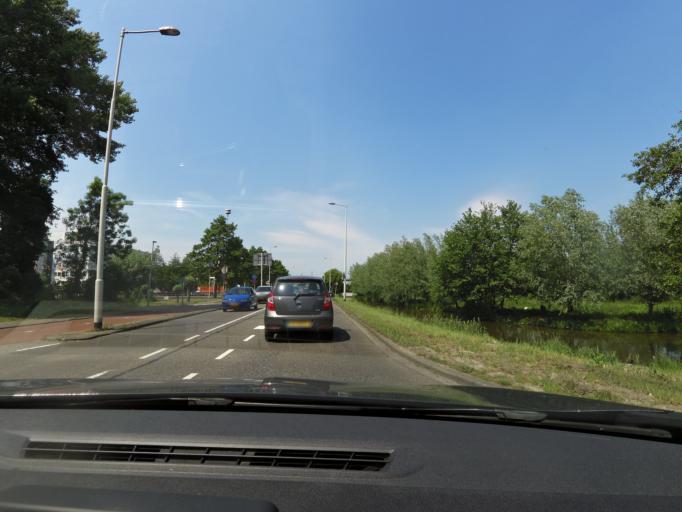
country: NL
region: South Holland
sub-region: Gemeente Rotterdam
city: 's-Gravenland
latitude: 51.9464
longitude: 4.5272
